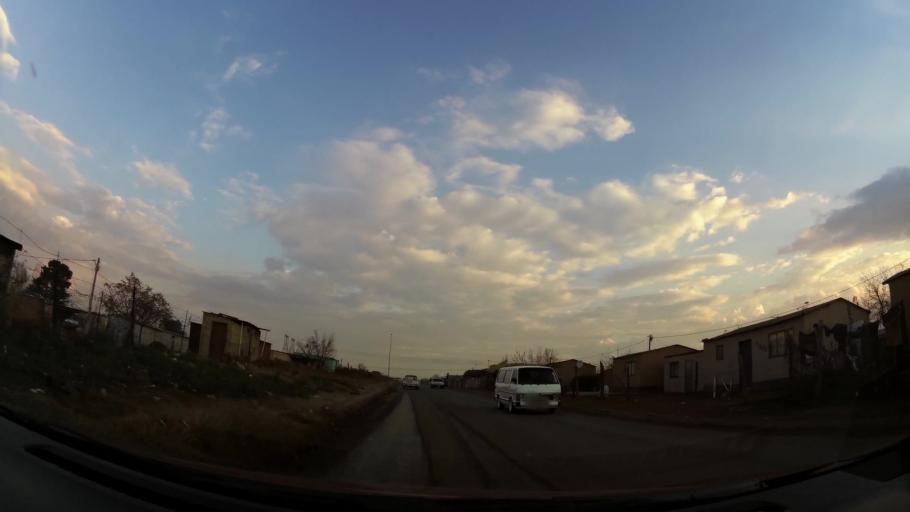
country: ZA
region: Gauteng
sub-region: City of Johannesburg Metropolitan Municipality
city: Orange Farm
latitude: -26.5528
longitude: 27.8400
